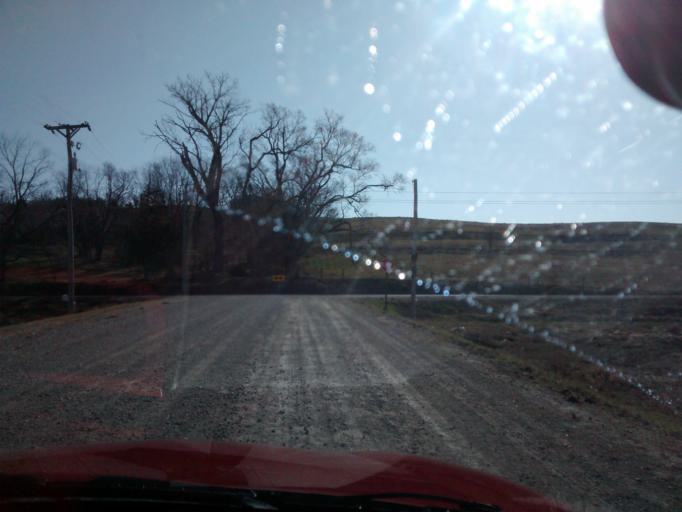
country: US
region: Iowa
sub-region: Pottawattamie County
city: Carter Lake
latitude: 41.3905
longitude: -95.8429
